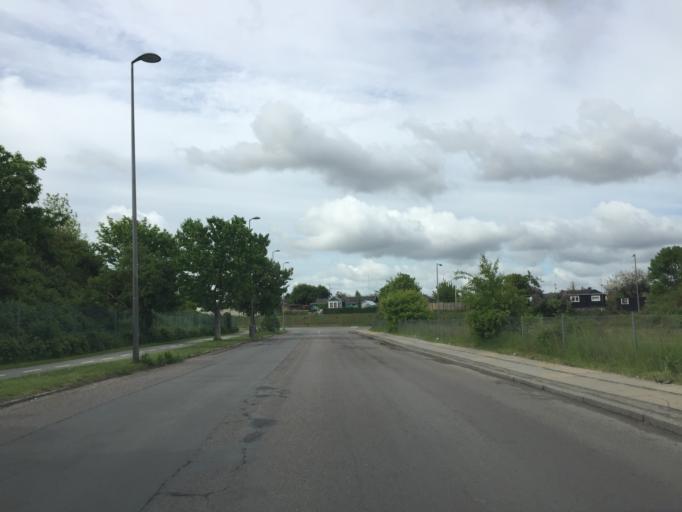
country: DK
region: Capital Region
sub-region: Kobenhavn
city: Christianshavn
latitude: 55.6796
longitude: 12.6183
